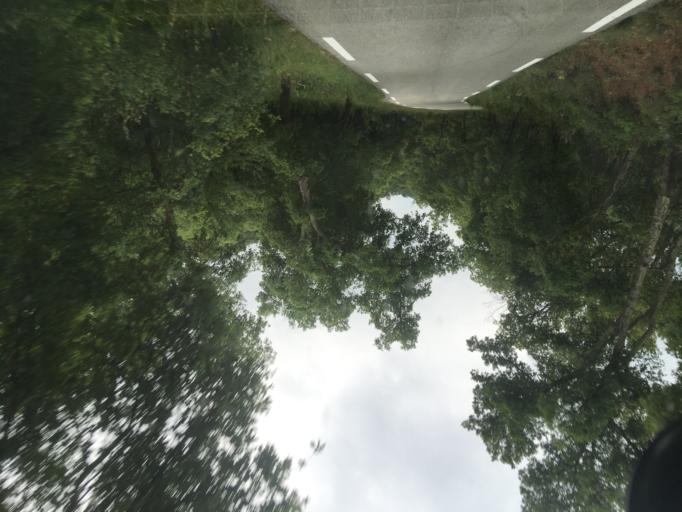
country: FR
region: Provence-Alpes-Cote d'Azur
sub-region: Departement du Var
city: Pignans
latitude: 43.2269
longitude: 6.2199
